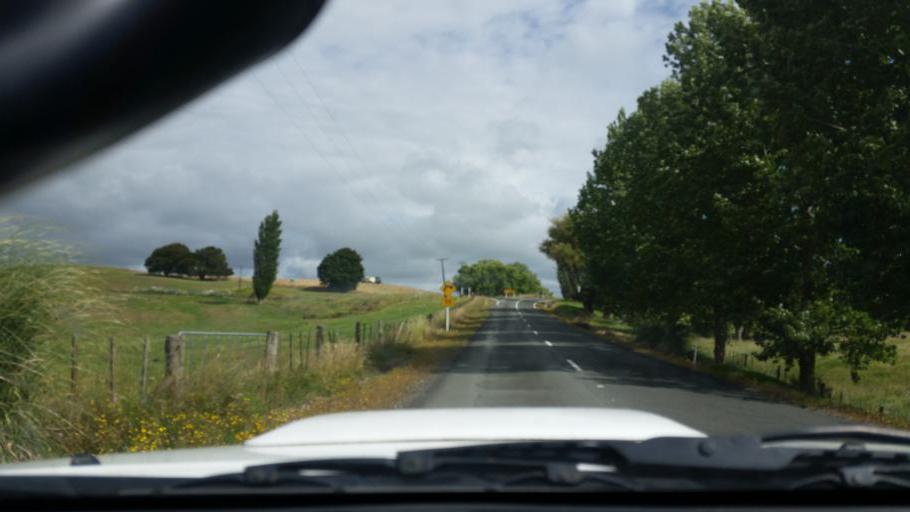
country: NZ
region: Auckland
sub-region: Auckland
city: Wellsford
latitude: -36.1300
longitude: 174.3582
